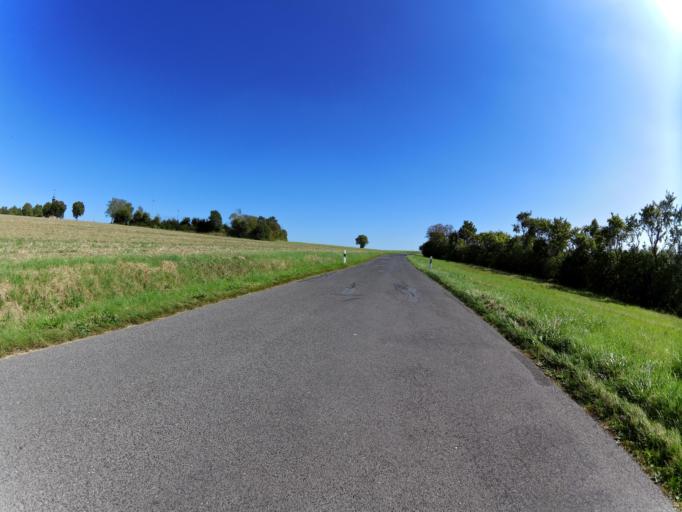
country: DE
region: Bavaria
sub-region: Regierungsbezirk Unterfranken
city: Kleinrinderfeld
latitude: 49.7004
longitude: 9.7849
